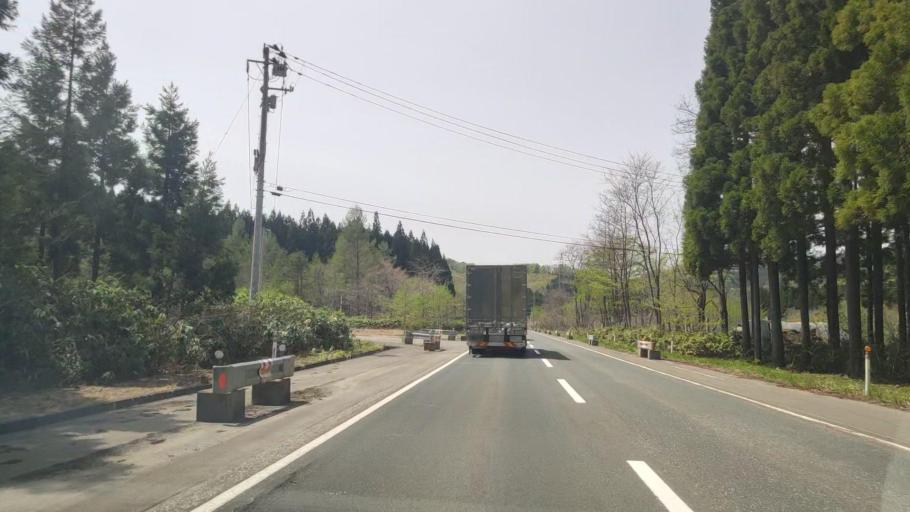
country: JP
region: Aomori
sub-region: Misawa Shi
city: Inuotose
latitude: 40.7872
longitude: 141.0797
